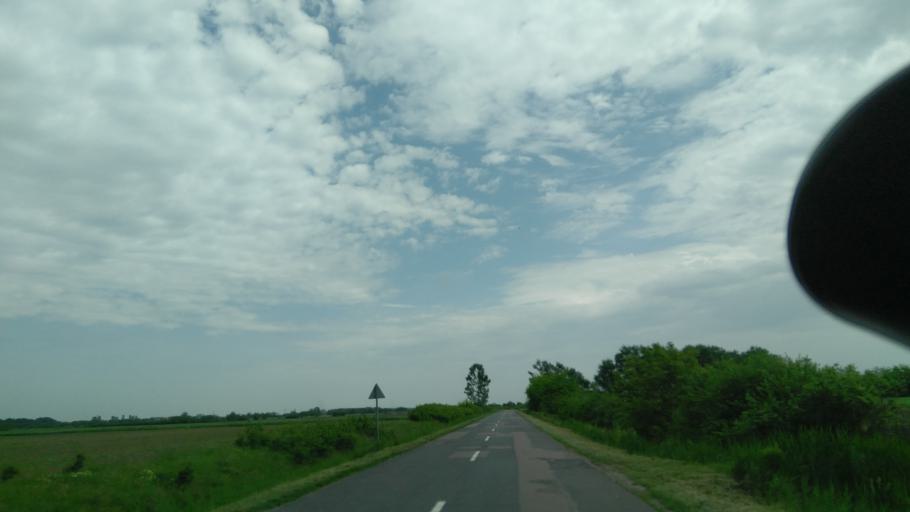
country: HU
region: Hajdu-Bihar
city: Komadi
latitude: 47.0233
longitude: 21.5671
